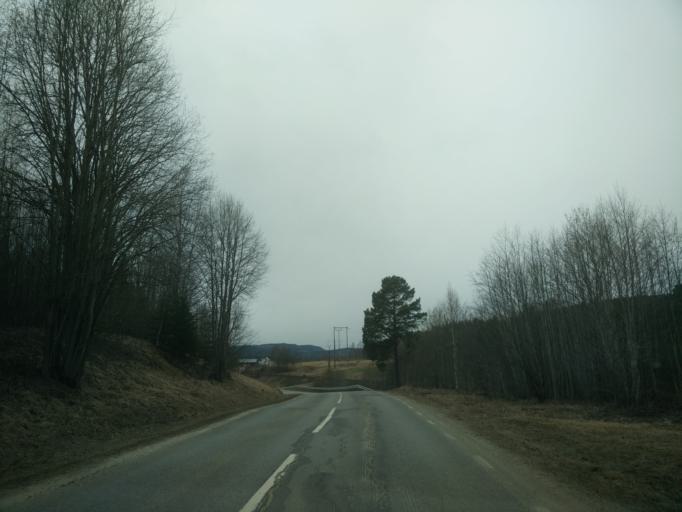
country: SE
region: Vaesternorrland
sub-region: Ange Kommun
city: Fransta
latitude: 62.4166
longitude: 16.5626
